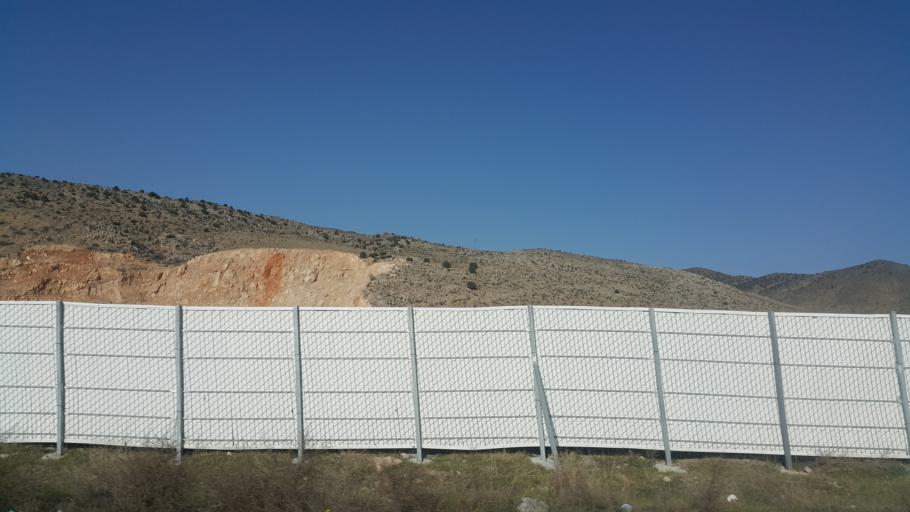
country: TR
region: Ankara
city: Sereflikochisar
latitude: 38.7628
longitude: 33.6552
